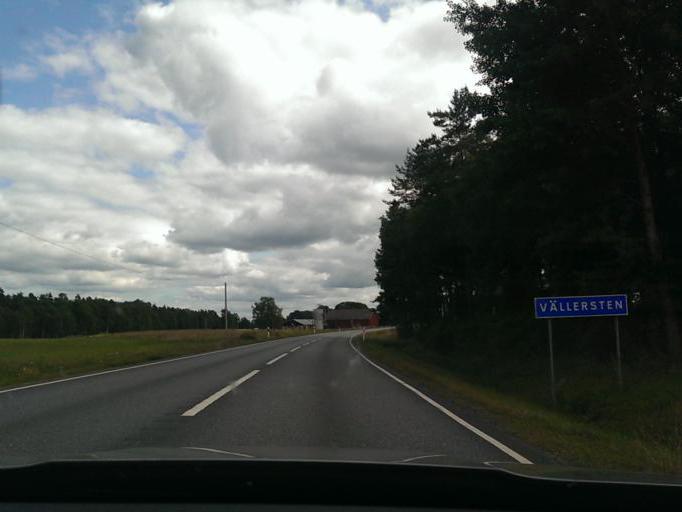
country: SE
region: Joenkoeping
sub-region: Varnamo Kommun
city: Varnamo
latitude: 57.2412
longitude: 14.0011
